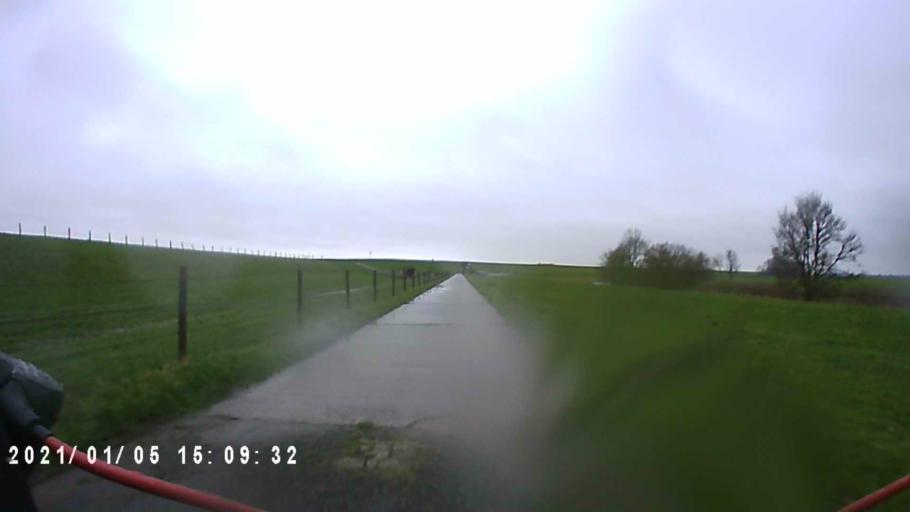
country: DE
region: Lower Saxony
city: Bunde
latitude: 53.2304
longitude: 7.2137
